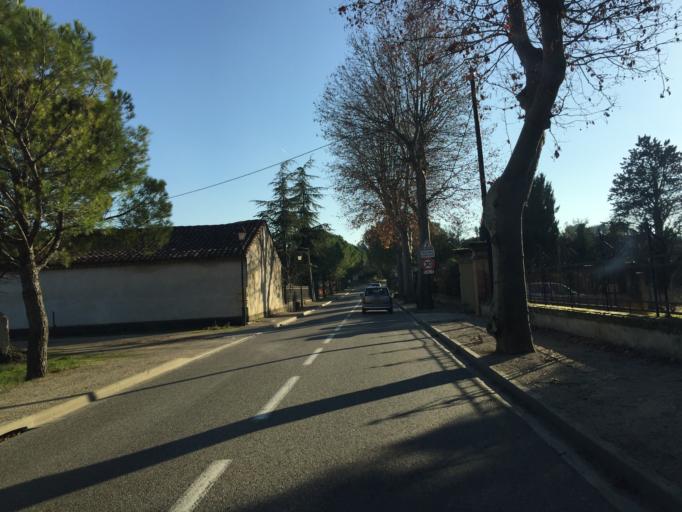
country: FR
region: Provence-Alpes-Cote d'Azur
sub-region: Departement du Vaucluse
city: Sainte-Cecile-les-Vignes
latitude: 44.2387
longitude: 4.8838
